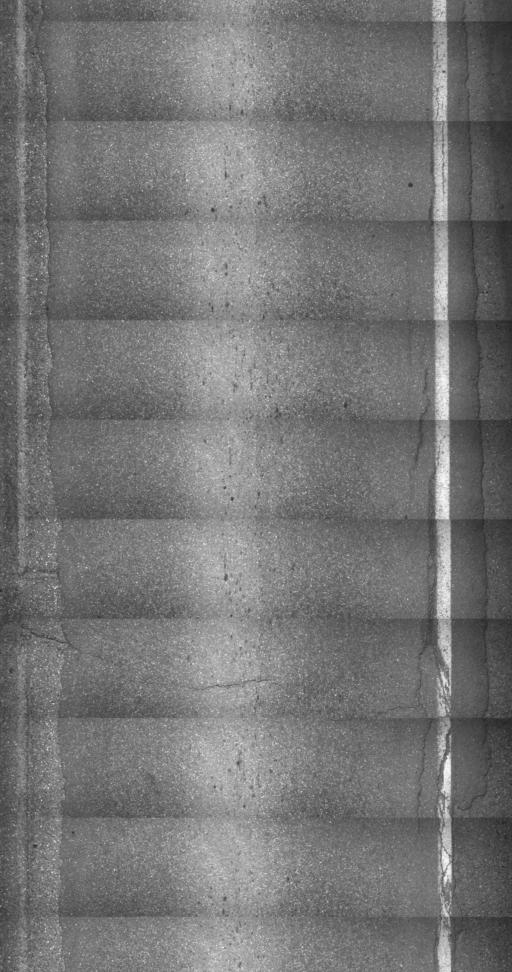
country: US
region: Vermont
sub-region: Caledonia County
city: Hardwick
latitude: 44.5158
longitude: -72.3758
